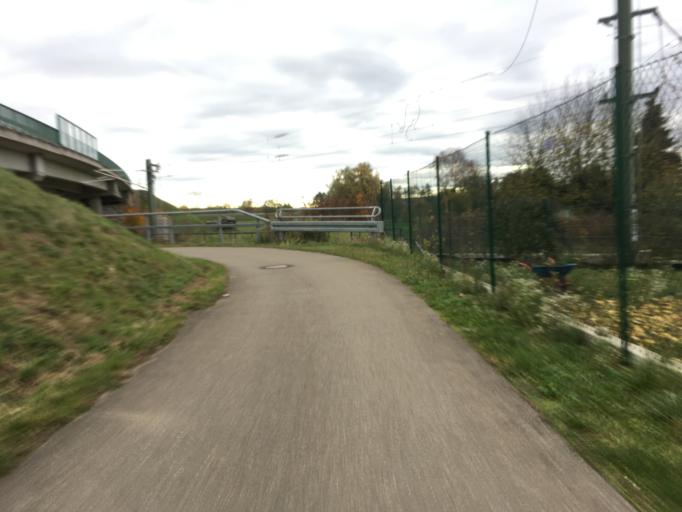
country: DE
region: Baden-Wuerttemberg
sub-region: Freiburg Region
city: Gottenheim
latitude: 48.0529
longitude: 7.7237
